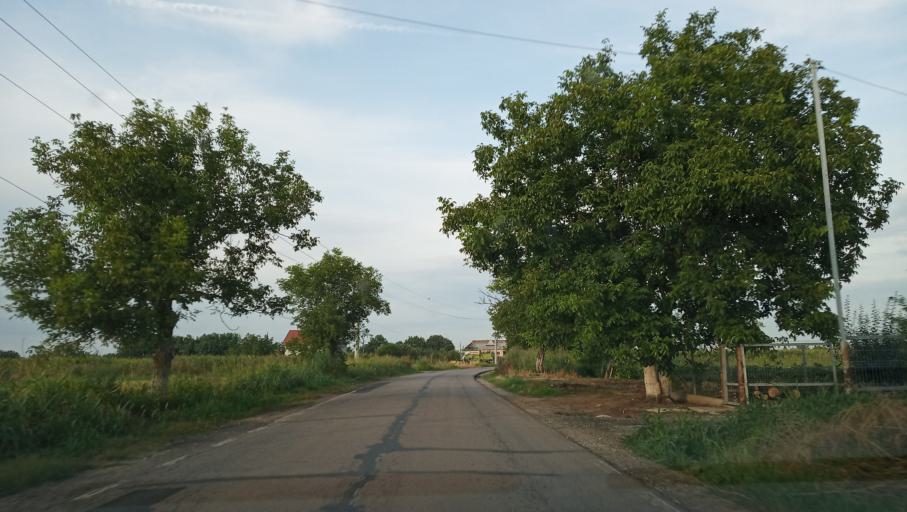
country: RO
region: Giurgiu
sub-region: Comuna Greaca
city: Greaca
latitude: 44.1102
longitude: 26.3235
